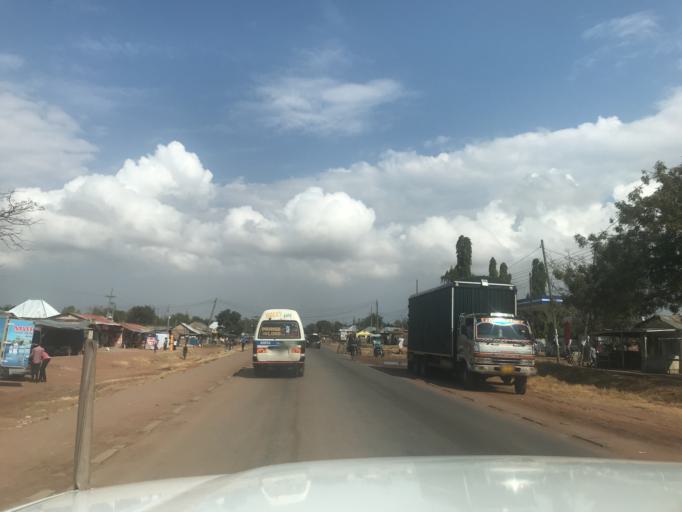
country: TZ
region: Mwanza
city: Usagara
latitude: -2.5554
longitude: 33.0453
